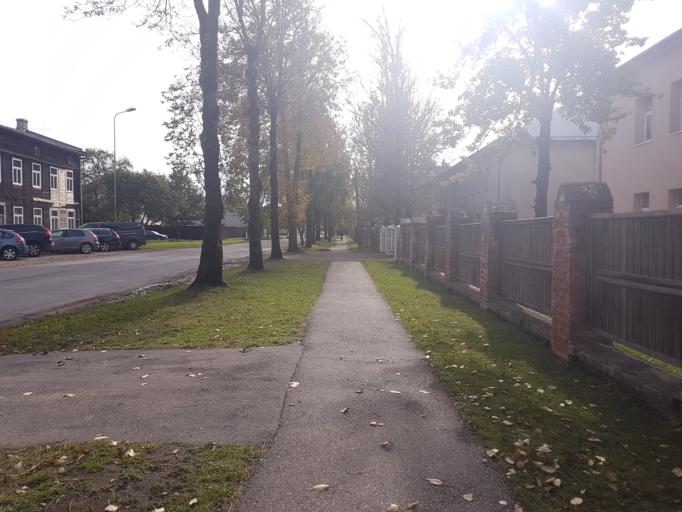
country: LV
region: Liepaja
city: Vec-Liepaja
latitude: 56.5259
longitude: 21.0116
